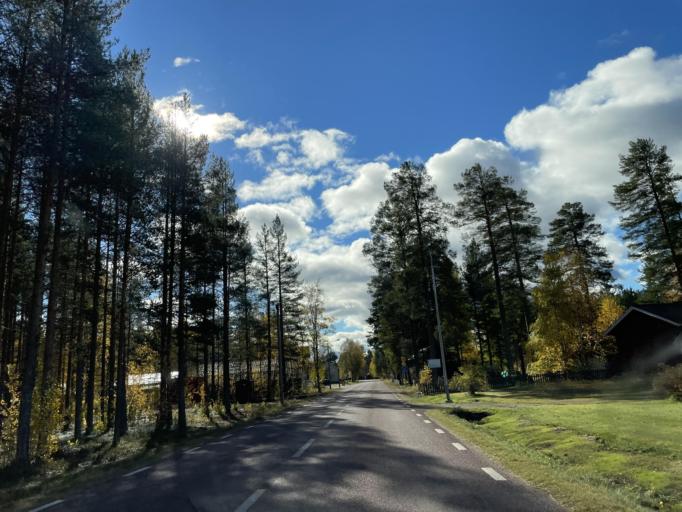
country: NO
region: Hedmark
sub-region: Trysil
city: Innbygda
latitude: 61.4118
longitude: 13.0841
